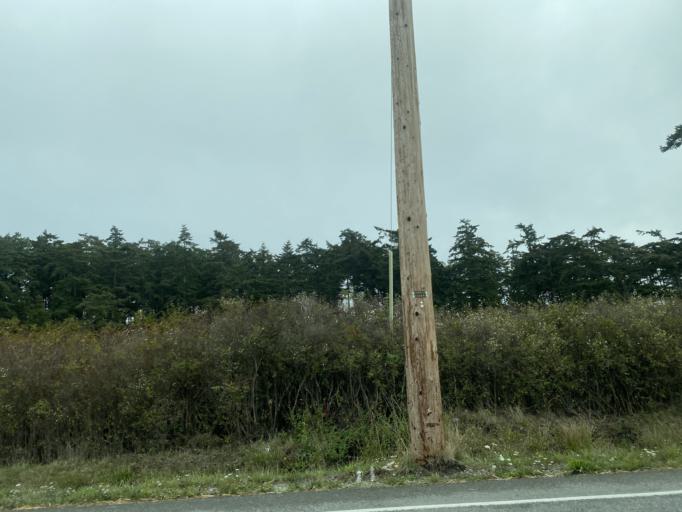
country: US
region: Washington
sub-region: Island County
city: Coupeville
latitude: 48.2112
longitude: -122.6930
